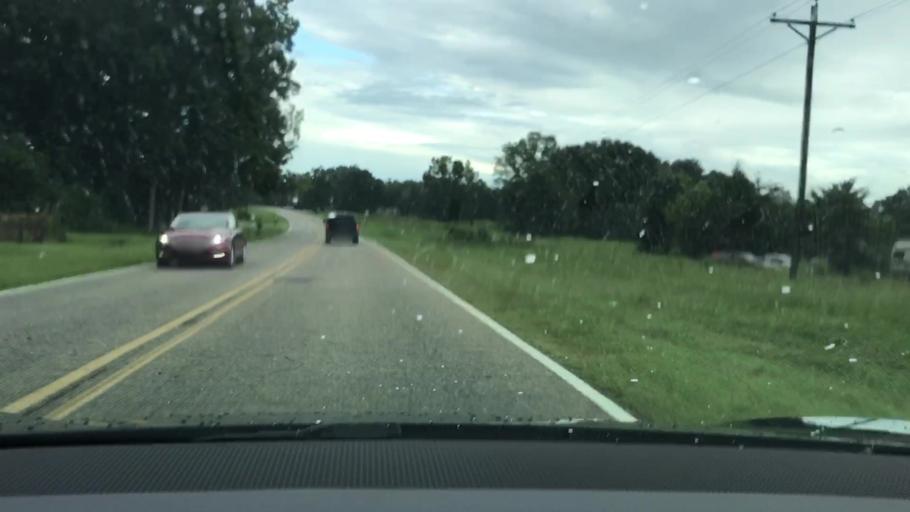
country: US
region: Alabama
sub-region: Geneva County
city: Samson
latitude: 31.1190
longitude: -86.1229
